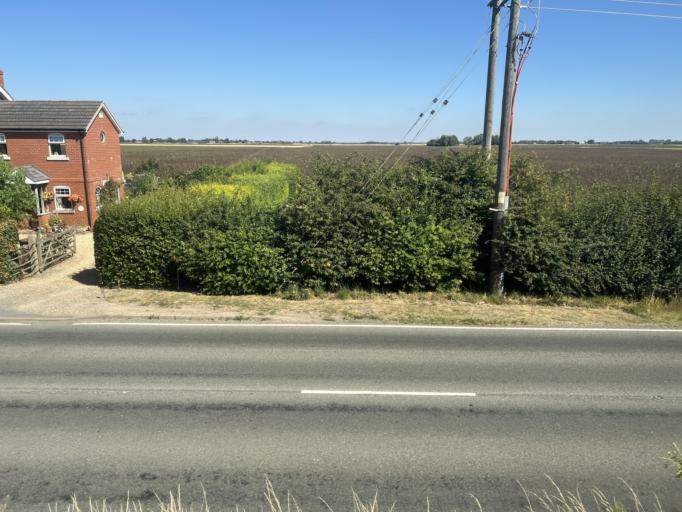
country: GB
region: England
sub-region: Lincolnshire
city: Kirton
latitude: 52.9751
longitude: -0.1023
